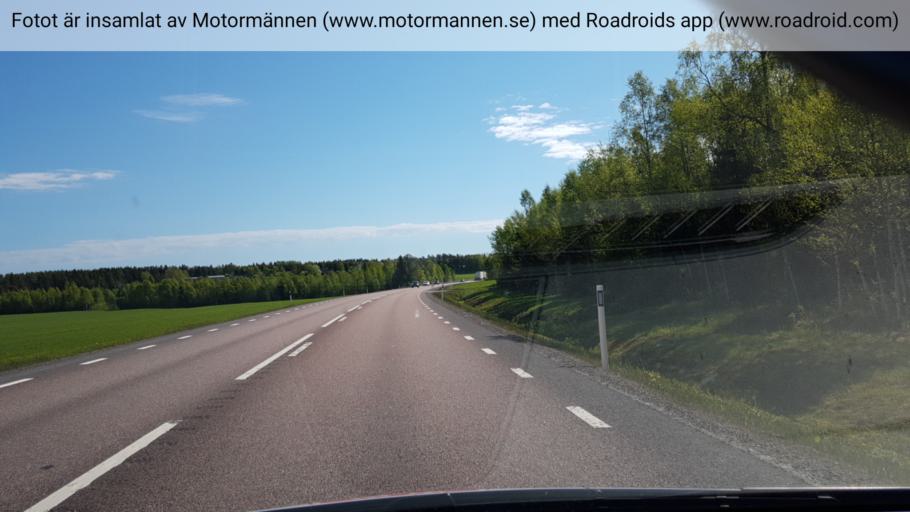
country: SE
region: Vaesterbotten
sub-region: Skelleftea Kommun
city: Burea
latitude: 64.3342
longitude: 21.2146
